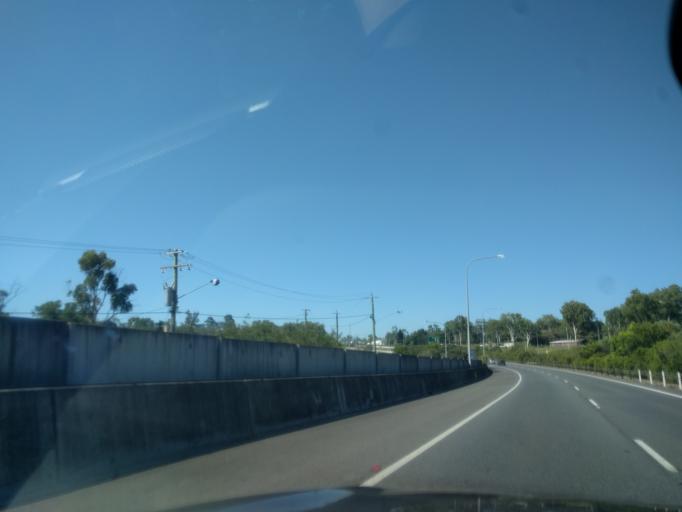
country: AU
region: Queensland
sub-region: Logan
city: Park Ridge South
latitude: -27.7127
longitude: 153.0357
